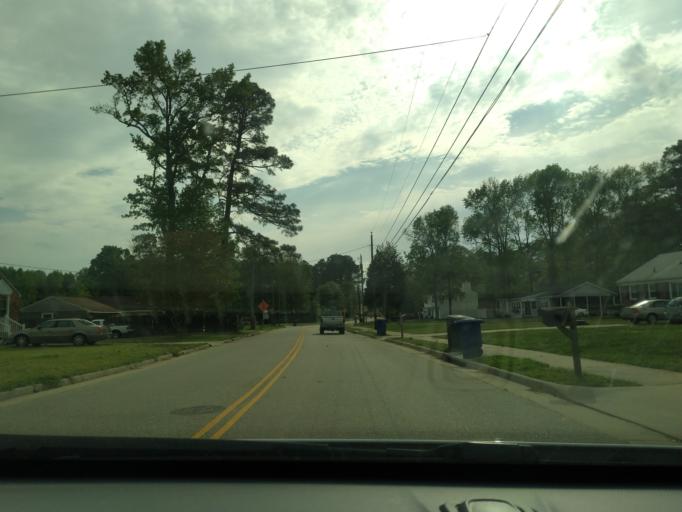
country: US
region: Virginia
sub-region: York County
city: Yorktown
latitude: 37.1683
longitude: -76.5192
